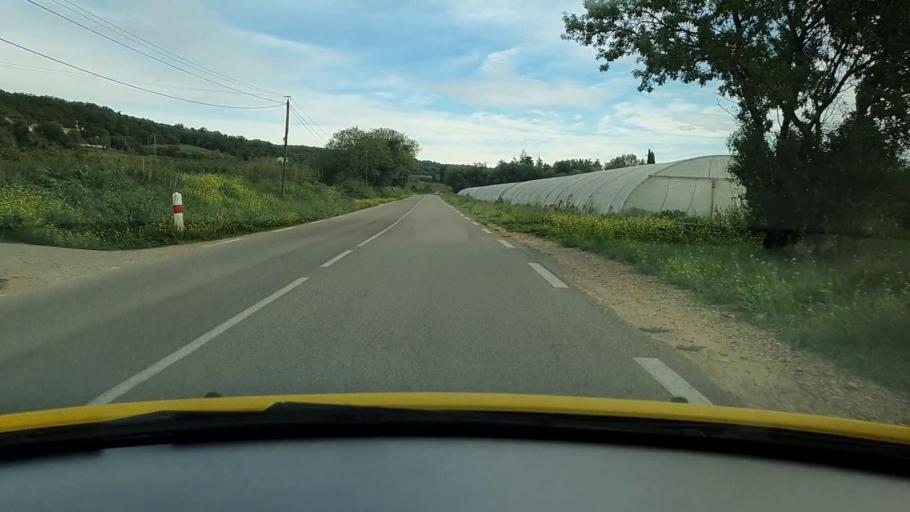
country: FR
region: Languedoc-Roussillon
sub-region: Departement du Gard
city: Bellegarde
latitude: 43.7680
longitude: 4.5324
